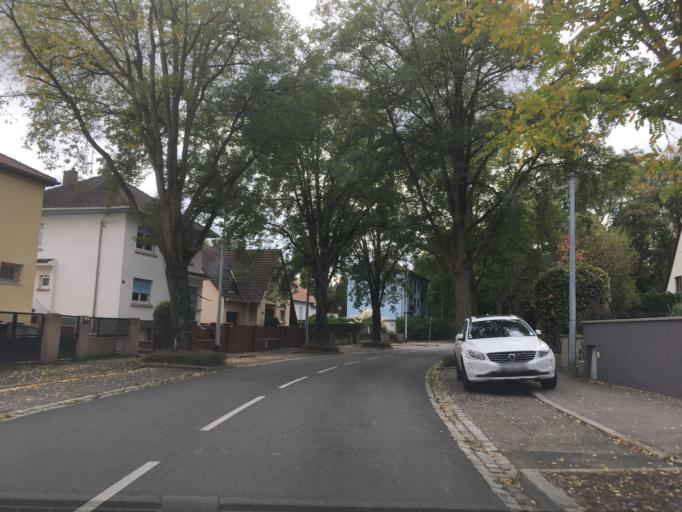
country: FR
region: Alsace
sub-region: Departement du Bas-Rhin
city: Illkirch-Graffenstaden
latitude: 48.5311
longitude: 7.7616
